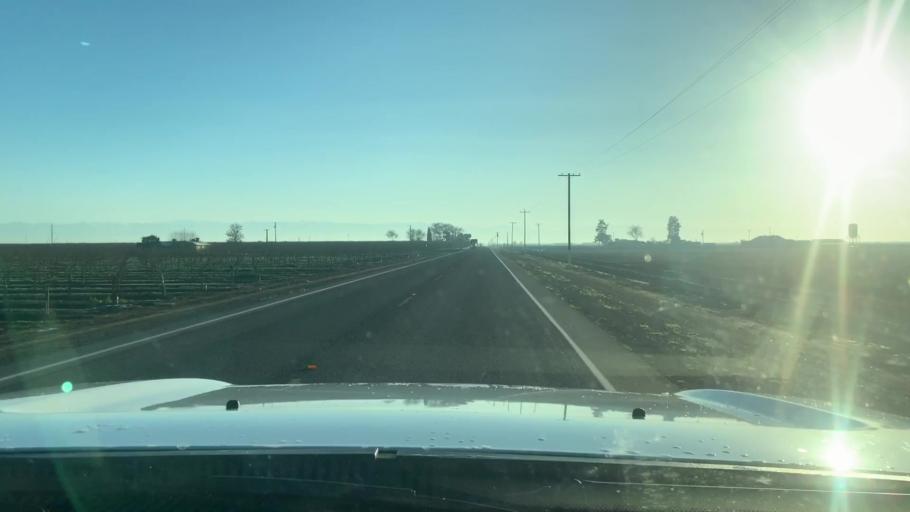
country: US
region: California
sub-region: Kings County
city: Home Garden
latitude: 36.2109
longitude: -119.5861
